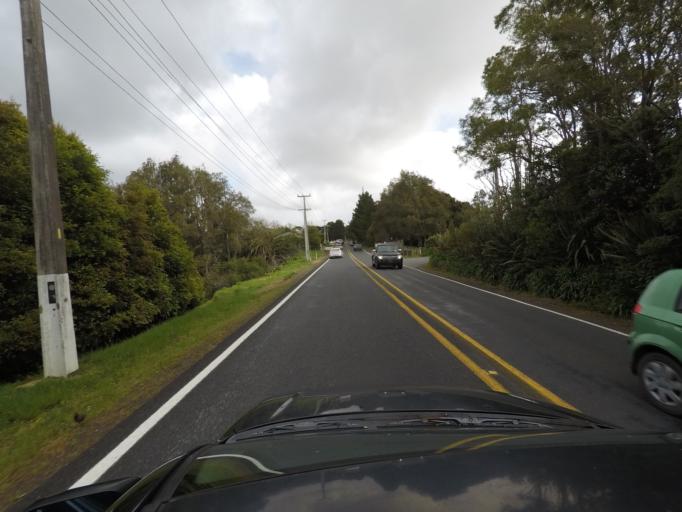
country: NZ
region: Auckland
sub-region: Auckland
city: Pakuranga
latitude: -36.9391
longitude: 174.9462
